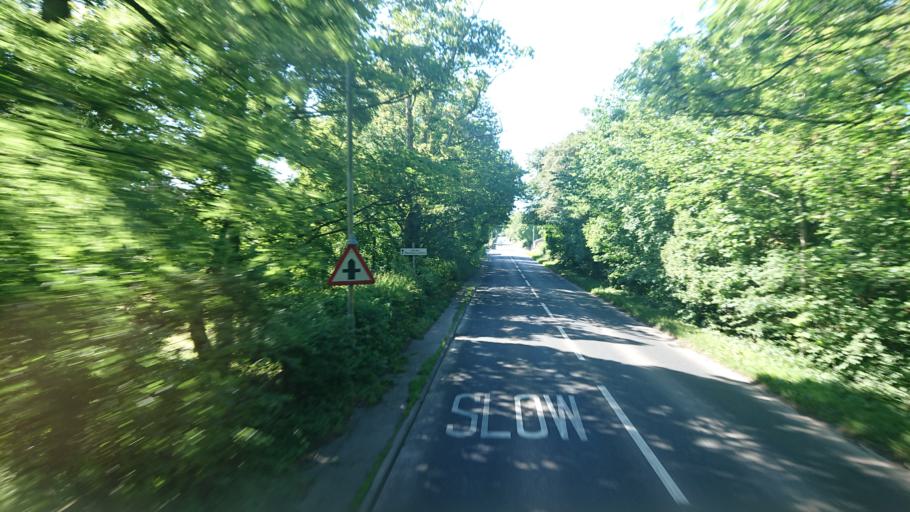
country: GB
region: England
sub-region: Lancashire
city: Bay Horse
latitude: 53.9687
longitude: -2.7807
